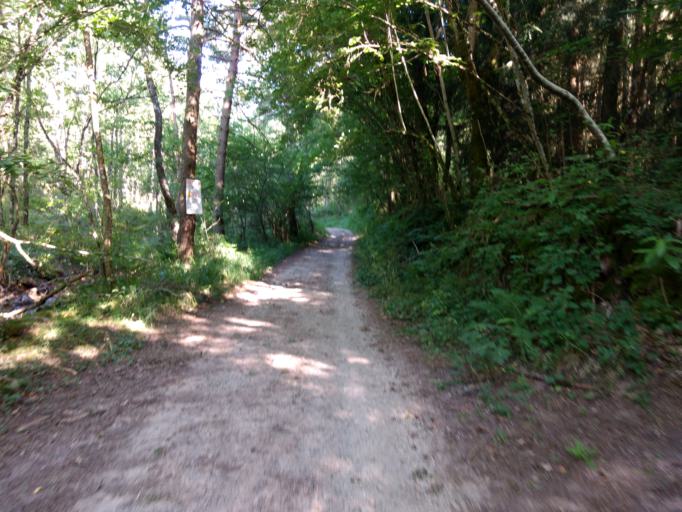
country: FR
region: Midi-Pyrenees
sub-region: Departement de l'Aveyron
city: La Loubiere
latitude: 44.3596
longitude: 2.6950
